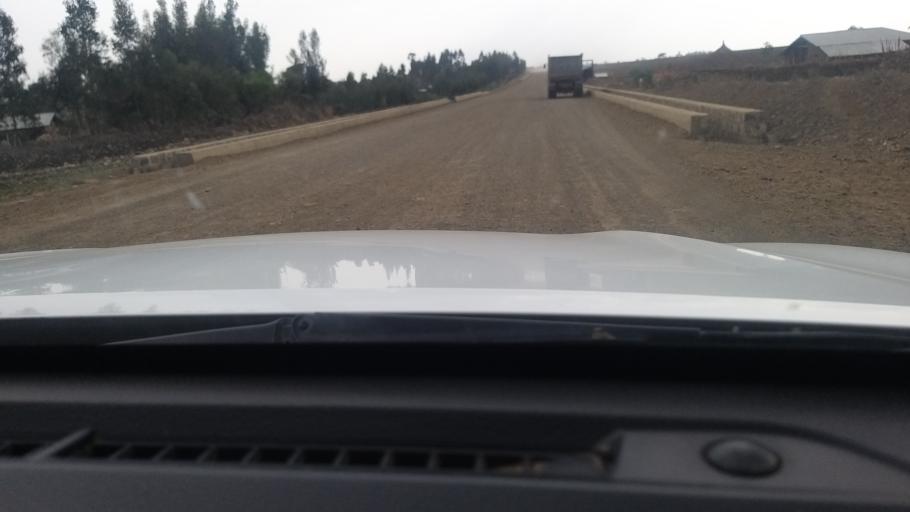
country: ET
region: Amhara
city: Were Ilu
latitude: 10.4502
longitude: 39.2050
